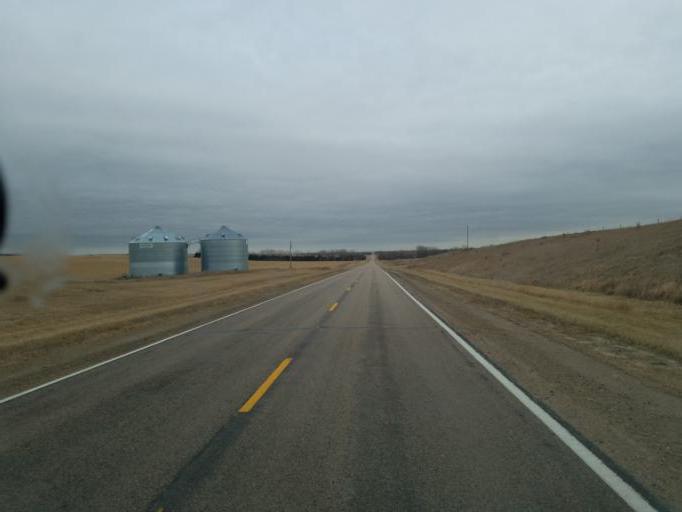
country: US
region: Nebraska
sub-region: Knox County
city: Bloomfield
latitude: 42.6127
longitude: -97.4777
